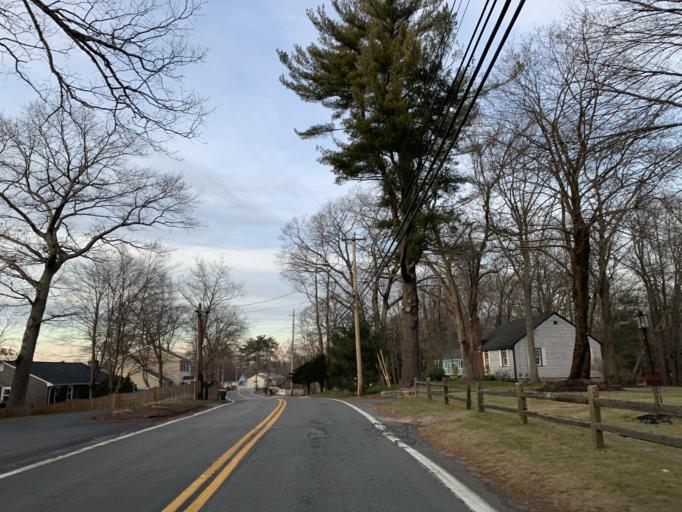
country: US
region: Rhode Island
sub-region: Providence County
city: Pascoag
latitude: 41.9409
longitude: -71.7043
